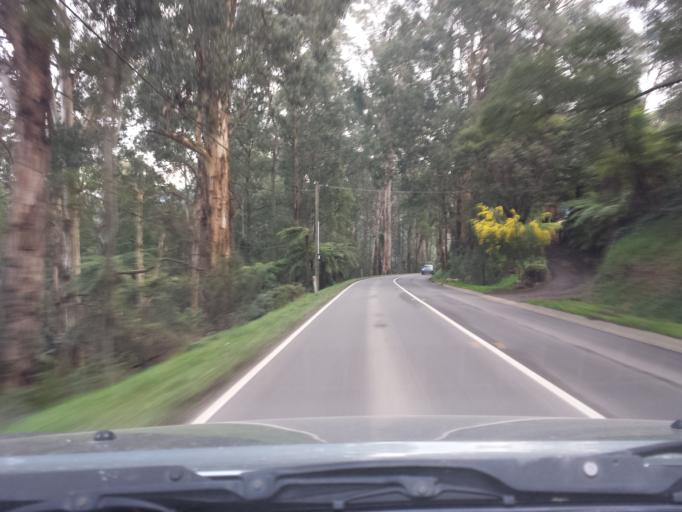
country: AU
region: Victoria
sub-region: Yarra Ranges
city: Monbulk
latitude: -37.8741
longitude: 145.4008
